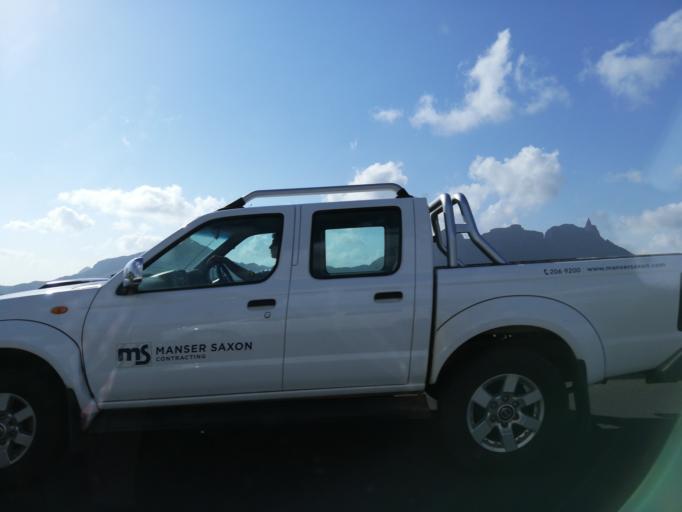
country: MU
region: Moka
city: Verdun
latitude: -20.2269
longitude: 57.5537
